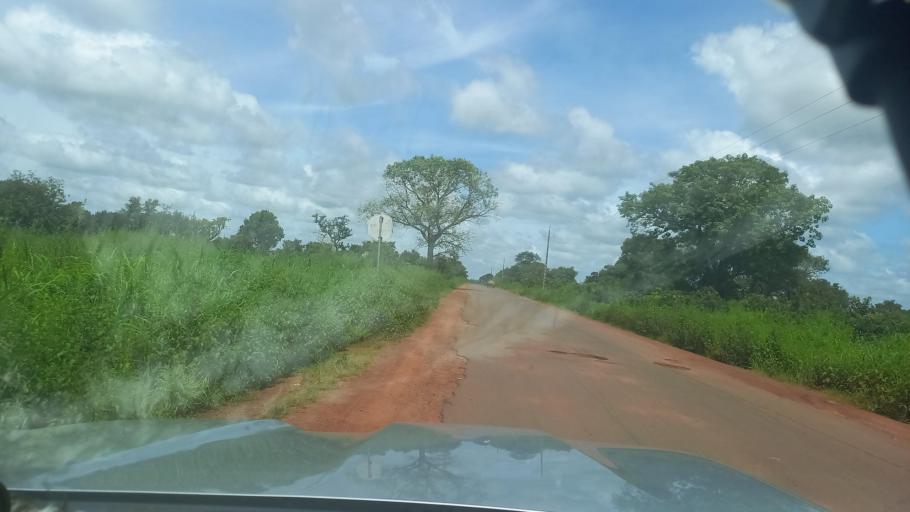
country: GM
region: Lower River
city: Kaiaf
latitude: 13.2238
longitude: -15.5399
